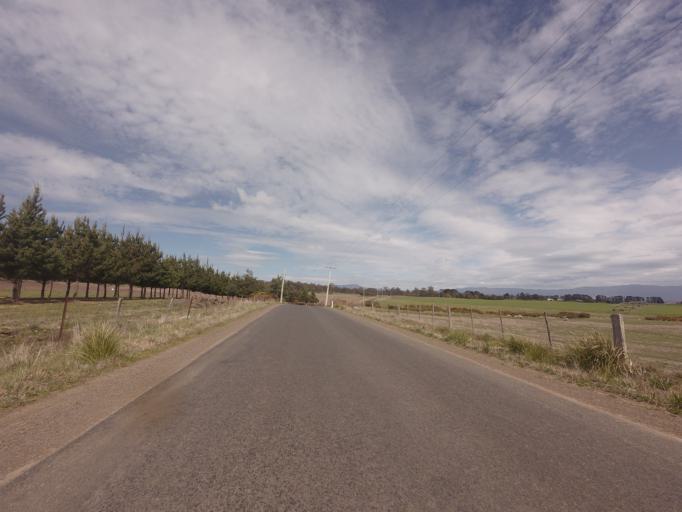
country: AU
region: Tasmania
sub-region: Northern Midlands
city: Longford
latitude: -41.7061
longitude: 147.1967
